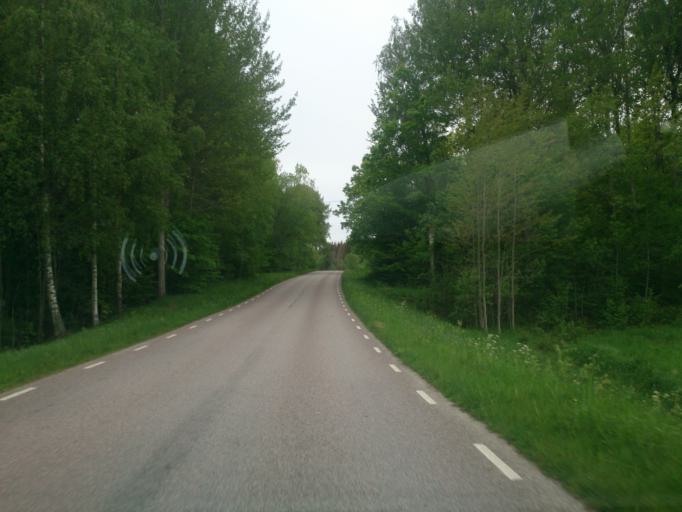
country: SE
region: OEstergoetland
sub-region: Atvidabergs Kommun
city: Atvidaberg
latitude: 58.3146
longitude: 16.0262
